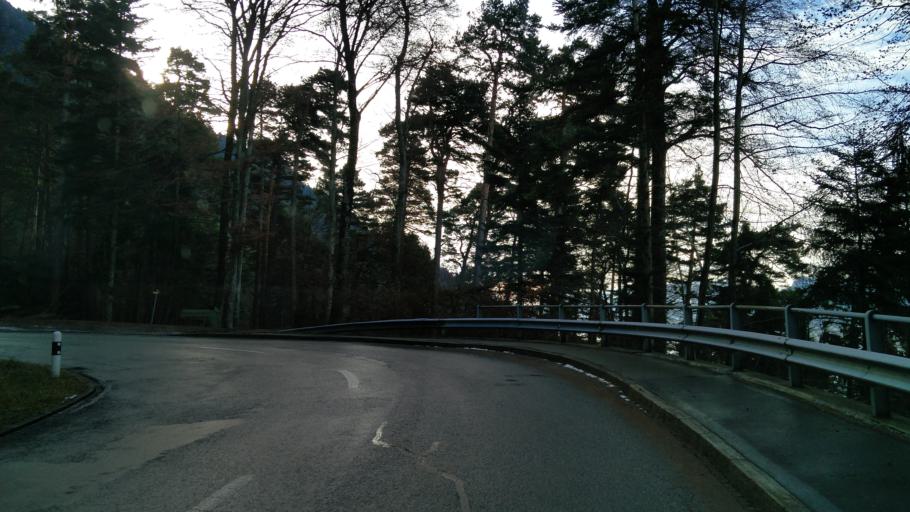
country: LI
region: Planken
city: Planken
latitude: 47.1792
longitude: 9.5377
